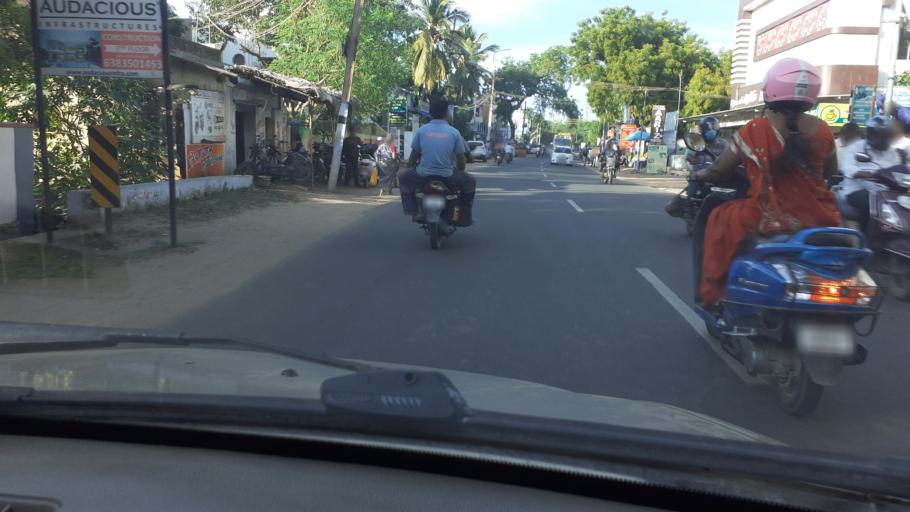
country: IN
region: Tamil Nadu
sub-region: Tirunelveli Kattabo
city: Tirunelveli
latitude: 8.7149
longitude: 77.7323
